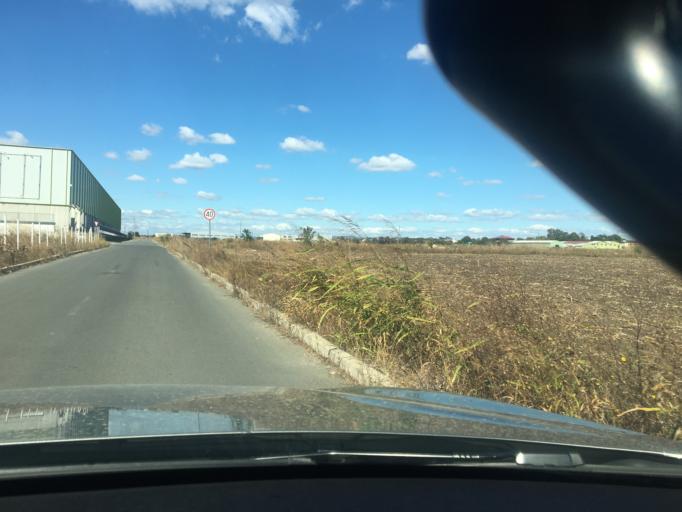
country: BG
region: Burgas
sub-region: Obshtina Burgas
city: Burgas
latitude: 42.5334
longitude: 27.4537
